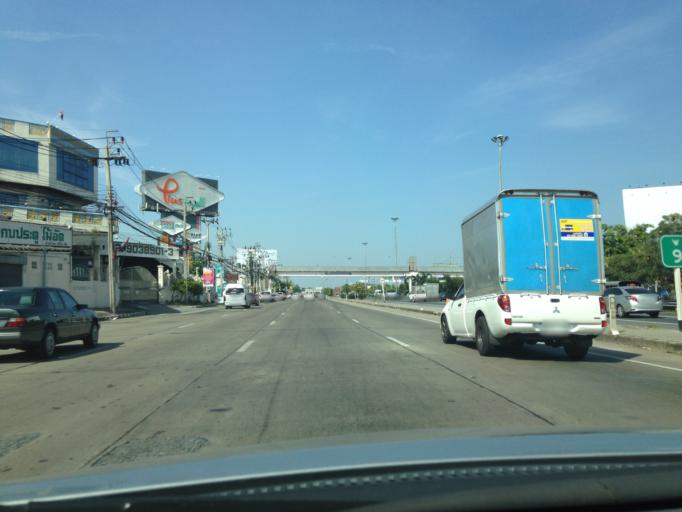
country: TH
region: Nonthaburi
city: Bang Yai
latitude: 13.8234
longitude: 100.4123
